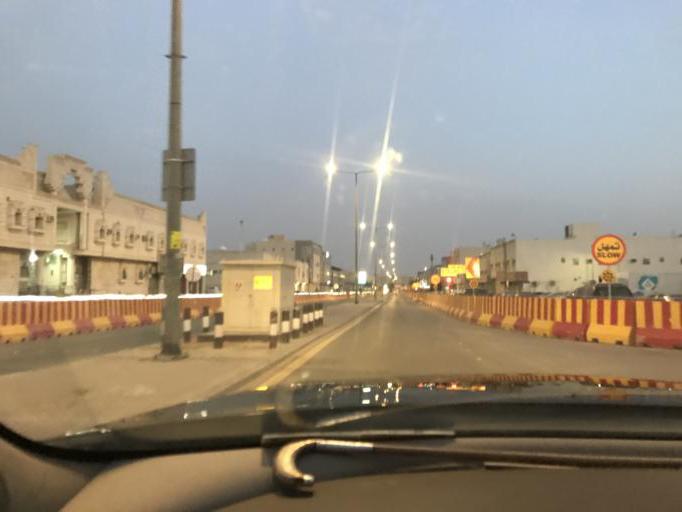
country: SA
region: Ar Riyad
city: Riyadh
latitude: 24.8026
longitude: 46.7067
